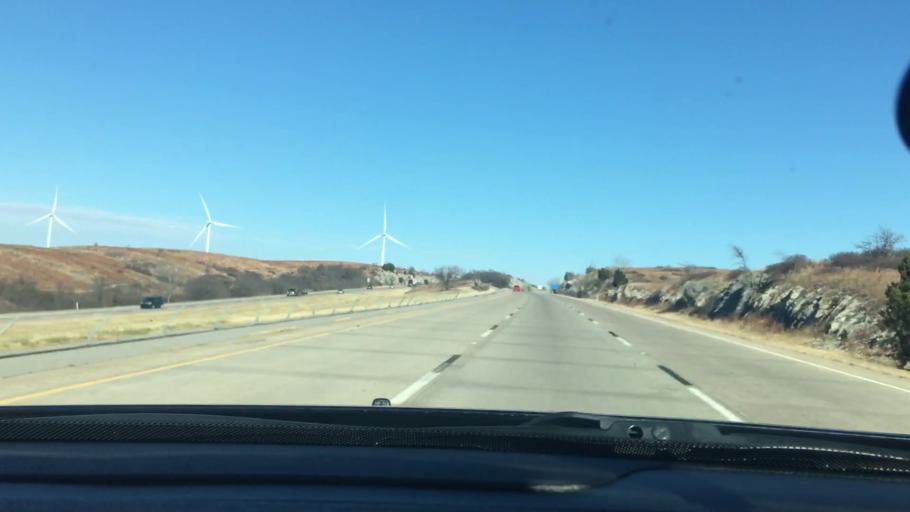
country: US
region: Oklahoma
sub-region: Murray County
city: Davis
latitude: 34.3662
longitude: -97.1464
